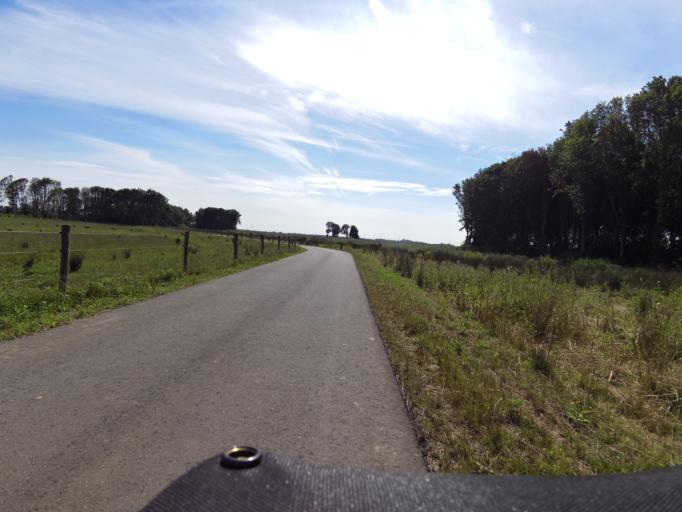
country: NL
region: South Holland
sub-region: Gemeente Hardinxveld-Giessendam
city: Neder-Hardinxveld
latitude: 51.7765
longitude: 4.8229
